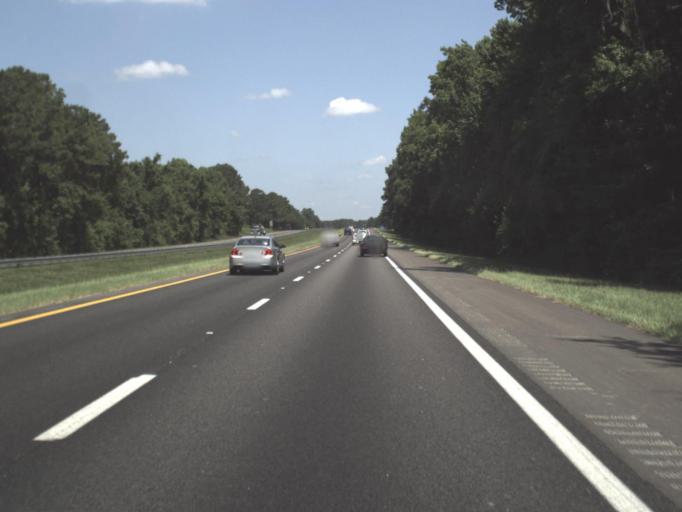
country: US
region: Florida
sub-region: Madison County
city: Madison
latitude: 30.4221
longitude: -83.4430
